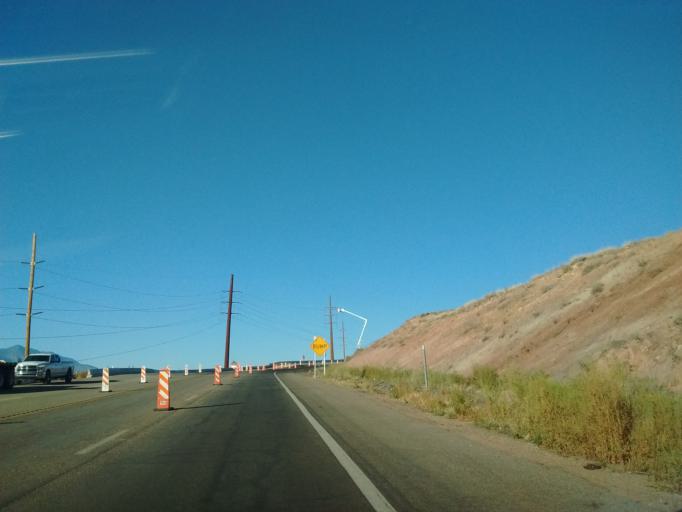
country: US
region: Utah
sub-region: Washington County
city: Washington
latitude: 37.1345
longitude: -113.4783
